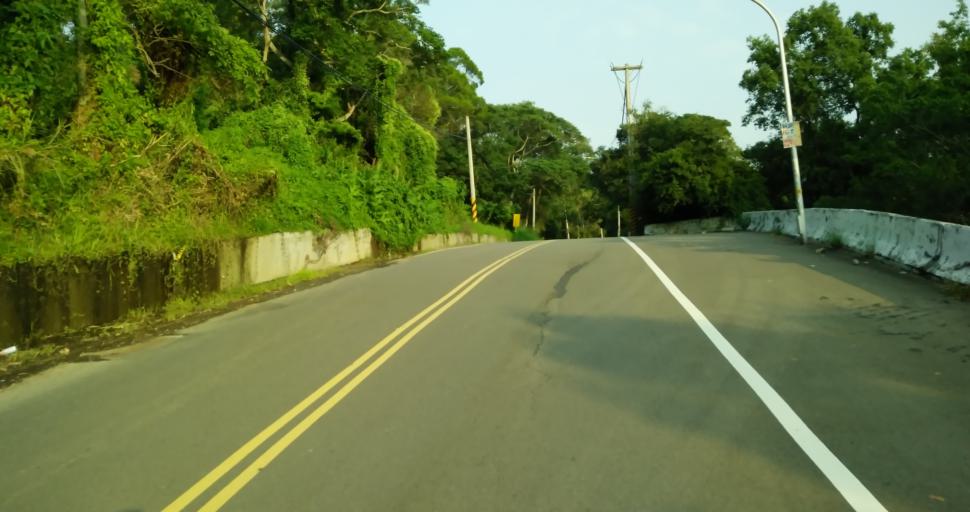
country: TW
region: Taiwan
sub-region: Hsinchu
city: Hsinchu
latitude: 24.7762
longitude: 120.9711
